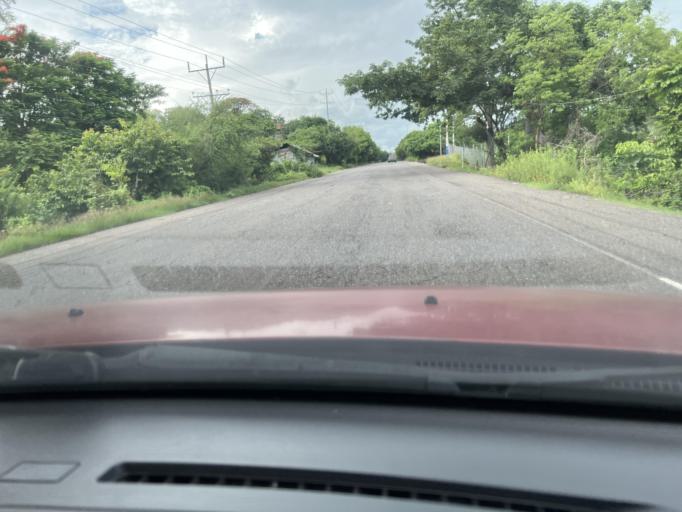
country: SV
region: La Union
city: San Alejo
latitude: 13.3955
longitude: -87.9000
